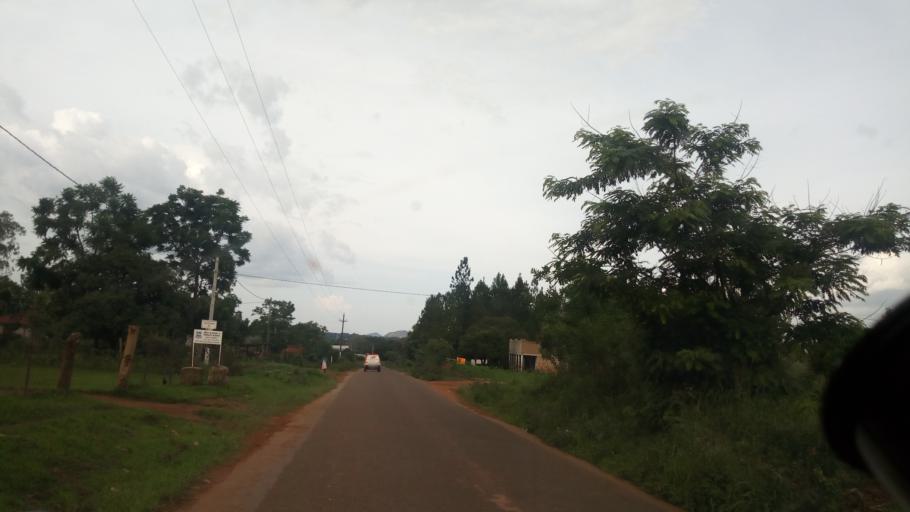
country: UG
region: Northern Region
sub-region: Lira District
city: Lira
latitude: 2.2574
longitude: 32.8513
